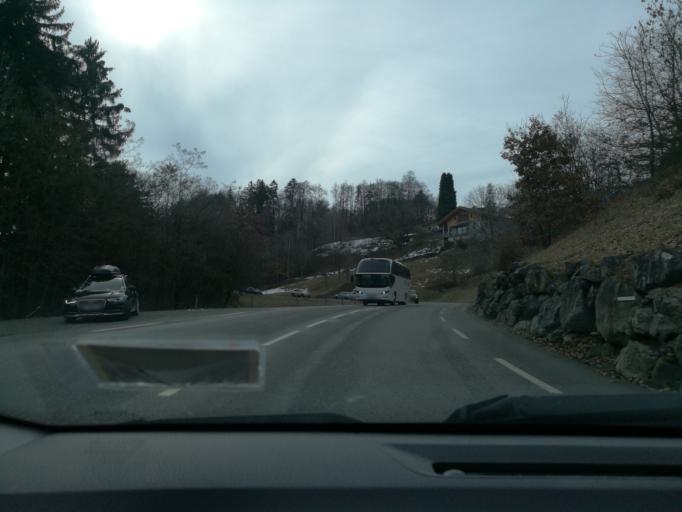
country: FR
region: Rhone-Alpes
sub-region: Departement de la Haute-Savoie
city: Domancy
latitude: 45.9245
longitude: 6.6334
